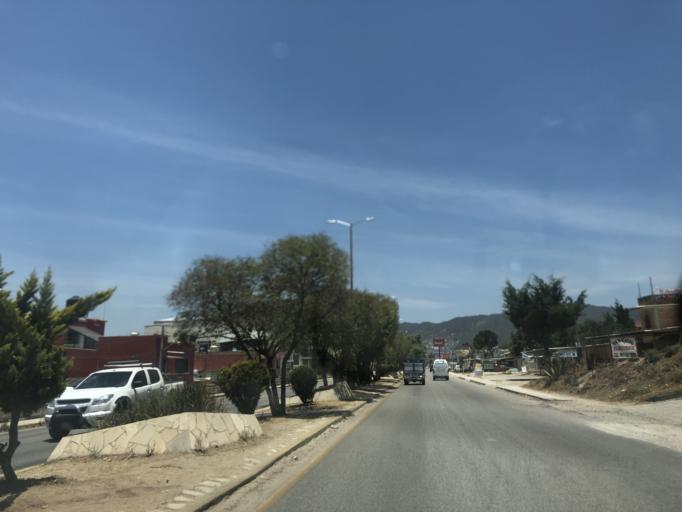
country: MX
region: Chiapas
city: San Cristobal de las Casas
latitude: 16.7226
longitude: -92.6343
